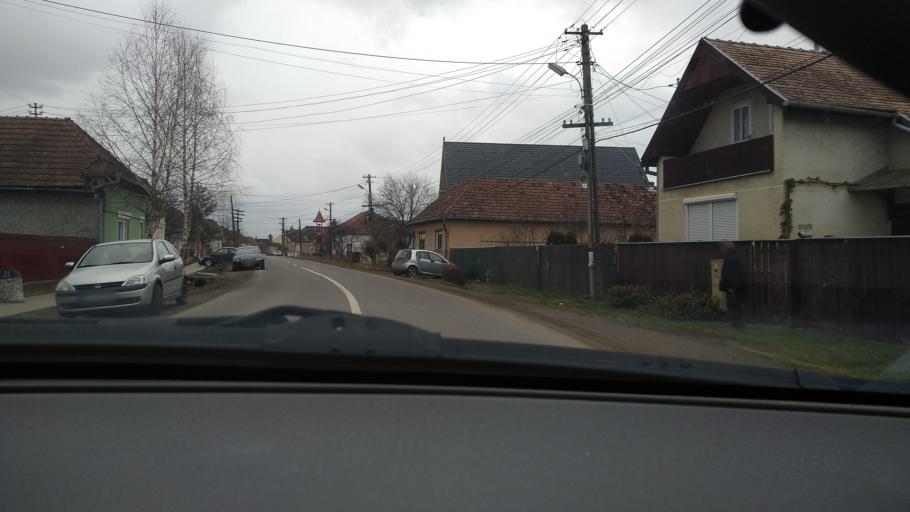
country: RO
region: Mures
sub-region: Comuna Miercurea Nirajului
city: Miercurea Nirajului
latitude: 46.5376
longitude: 24.8098
